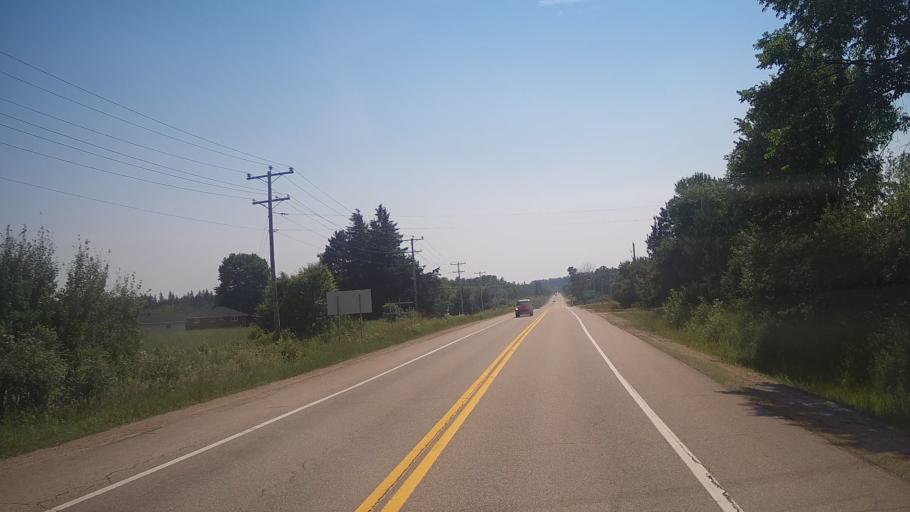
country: CA
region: Ontario
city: Pembroke
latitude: 45.8277
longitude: -77.0146
